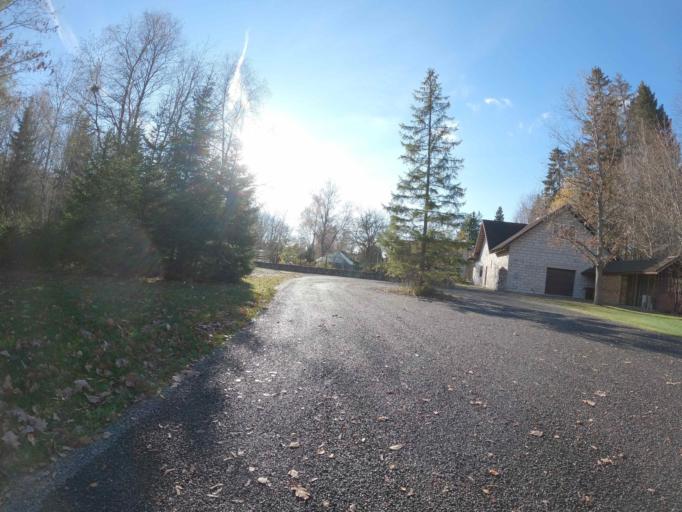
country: EE
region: Raplamaa
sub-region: Rapla vald
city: Rapla
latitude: 59.0048
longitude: 24.8085
